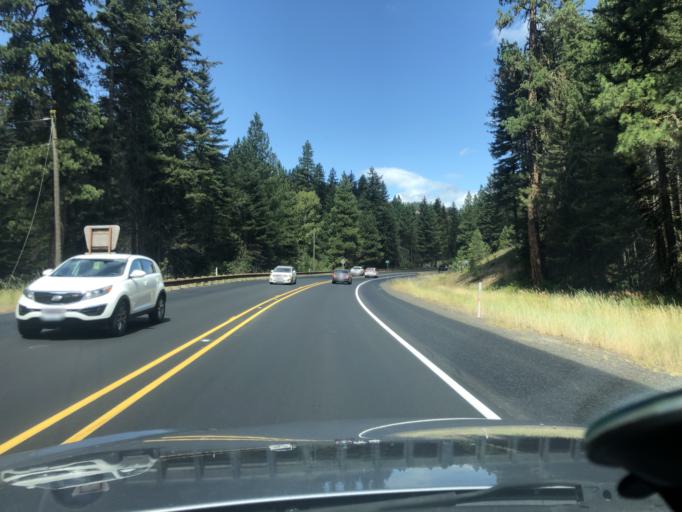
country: US
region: Washington
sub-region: Kittitas County
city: Cle Elum
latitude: 47.2912
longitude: -120.6997
